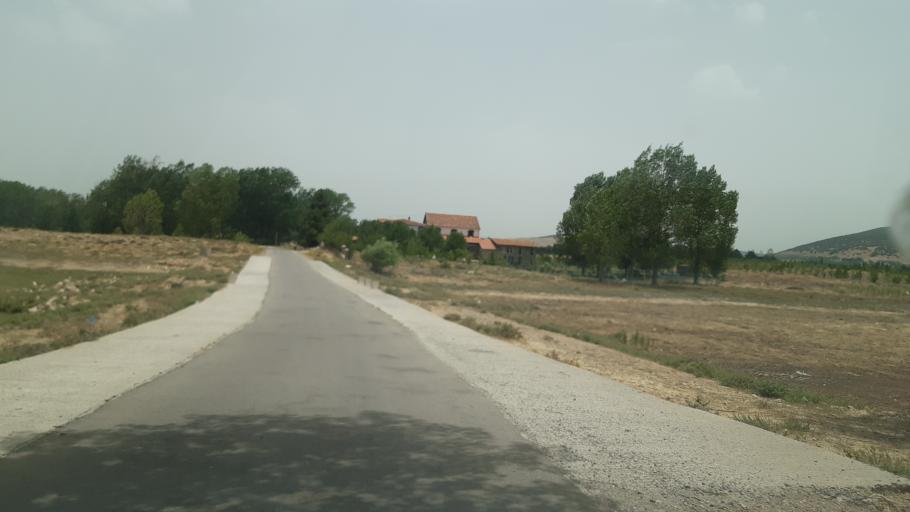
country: MA
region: Meknes-Tafilalet
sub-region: Ifrane
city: Ifrane
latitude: 33.6467
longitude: -5.0197
